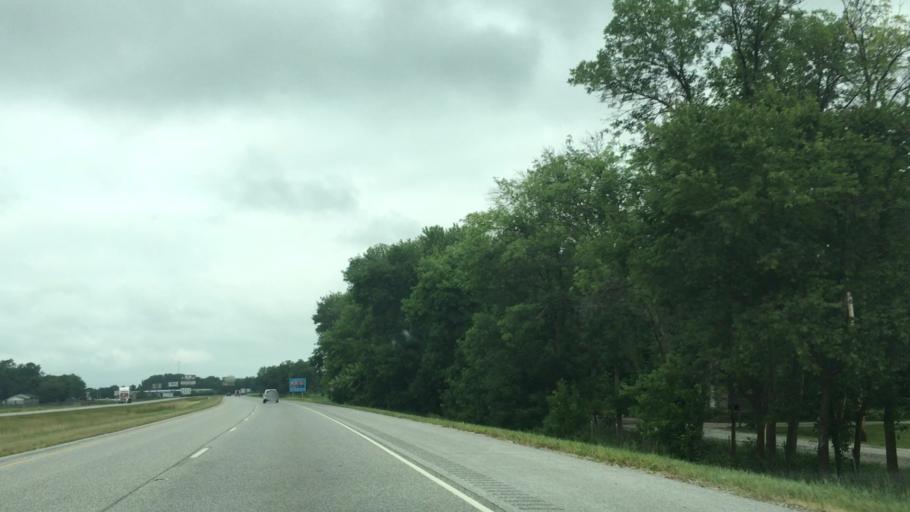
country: US
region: Illinois
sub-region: Rock Island County
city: Moline
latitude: 41.4578
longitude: -90.5149
